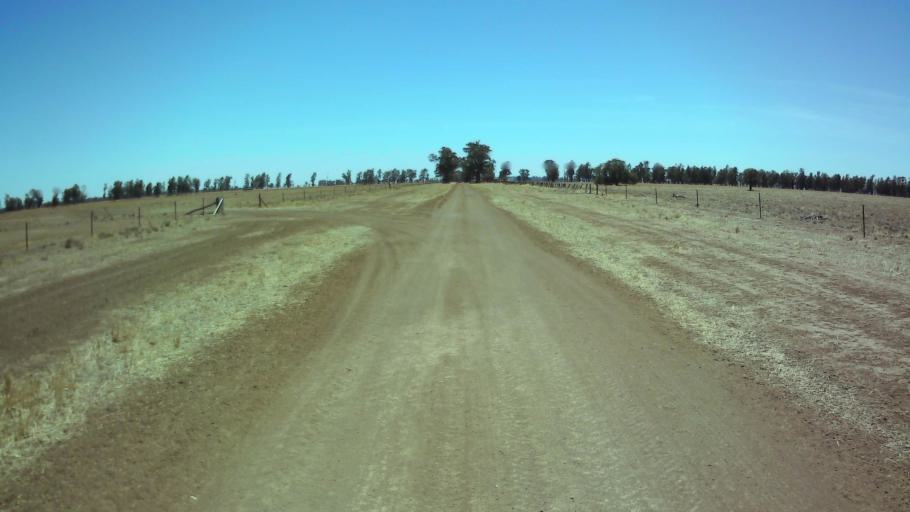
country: AU
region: New South Wales
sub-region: Weddin
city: Grenfell
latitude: -33.9748
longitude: 147.7373
